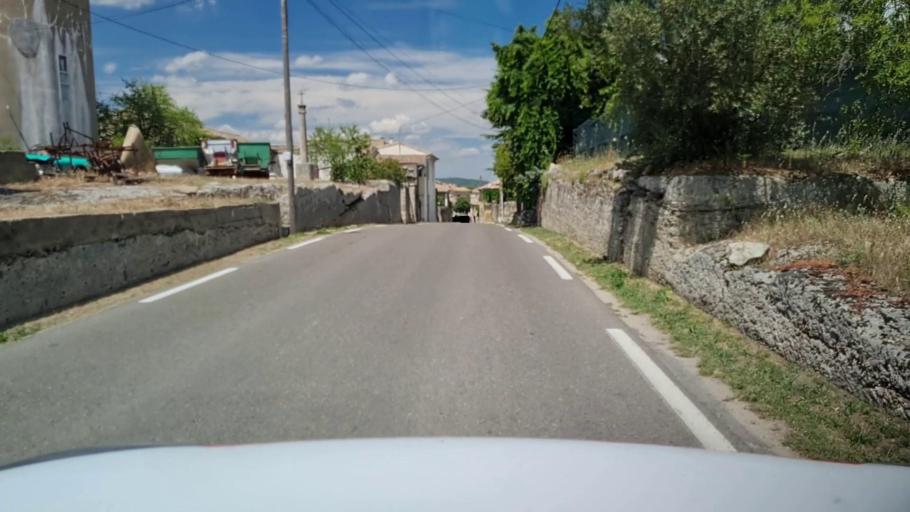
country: FR
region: Languedoc-Roussillon
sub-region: Departement du Gard
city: Villevieille
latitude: 43.8122
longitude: 4.1216
